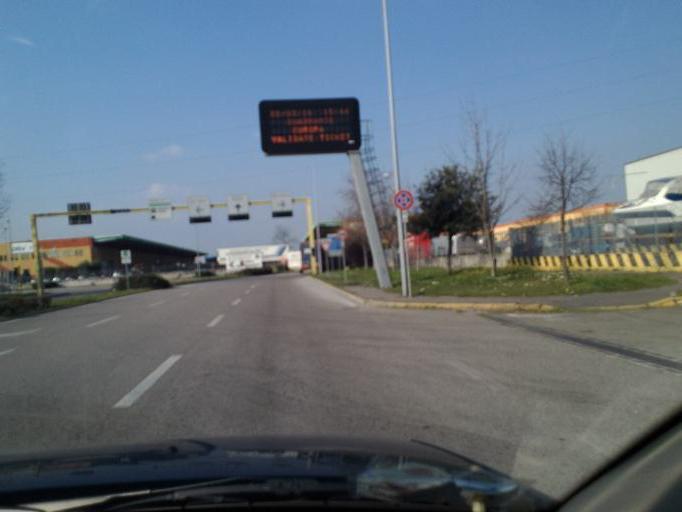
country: IT
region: Veneto
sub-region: Provincia di Verona
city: Dossobuono
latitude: 45.4175
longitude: 10.9293
